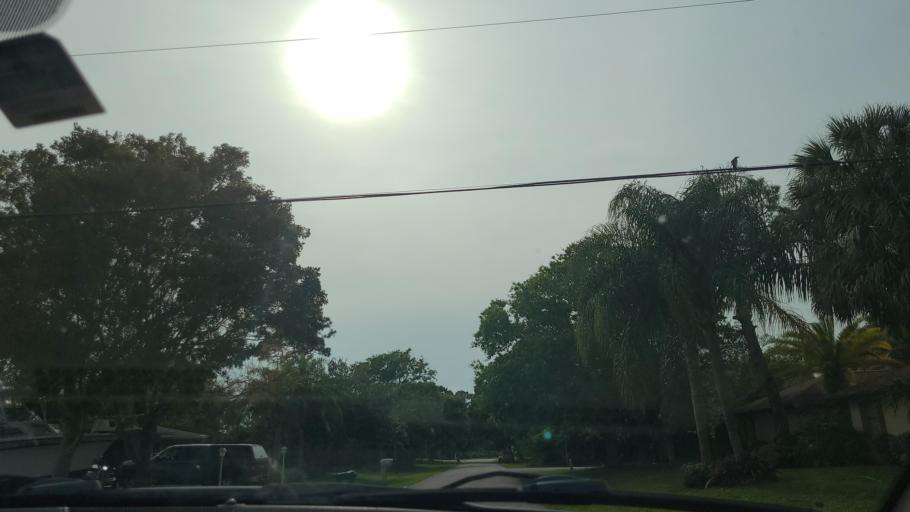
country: US
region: Florida
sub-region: Indian River County
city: Sebastian
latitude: 27.8105
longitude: -80.4820
